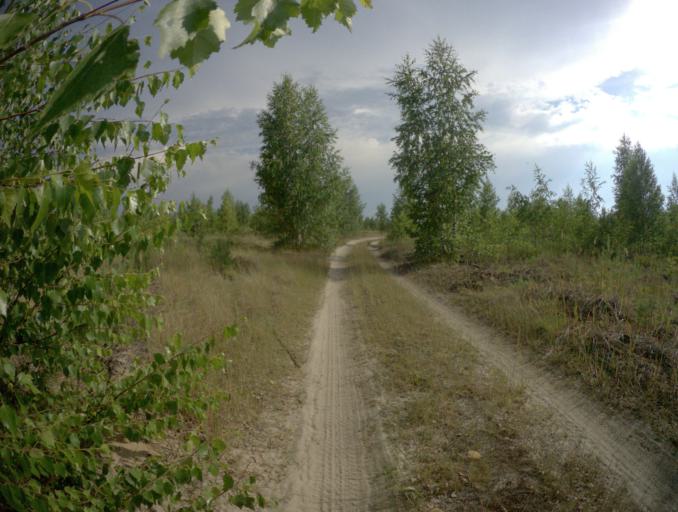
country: RU
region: Ivanovo
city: Talitsy
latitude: 56.4305
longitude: 42.3200
